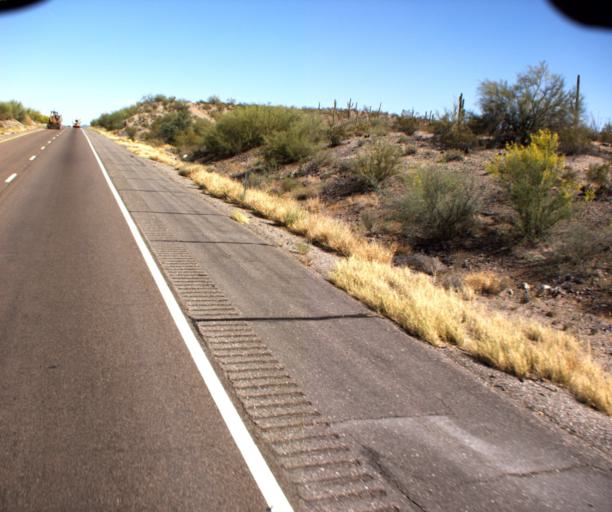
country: US
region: Arizona
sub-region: Pinal County
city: Maricopa
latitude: 32.8496
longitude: -112.3392
